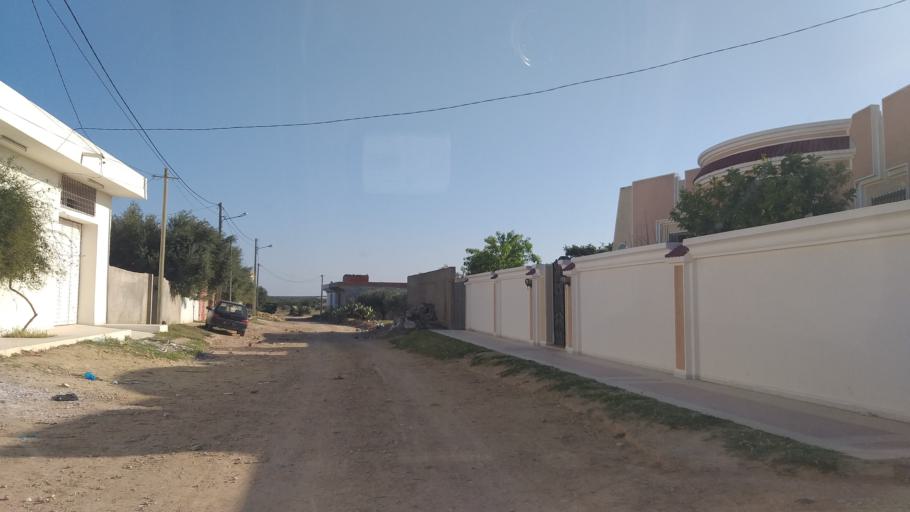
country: TN
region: Al Mahdiyah
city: El Jem
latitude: 35.2825
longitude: 10.7111
